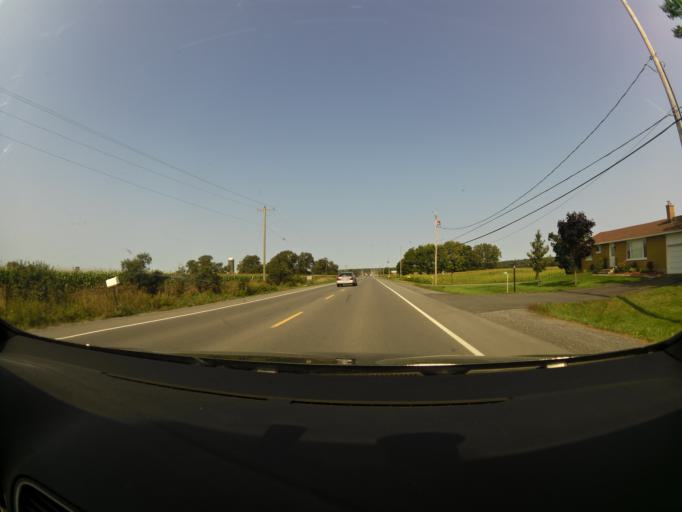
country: CA
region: Ontario
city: Bells Corners
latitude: 45.3301
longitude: -76.0175
